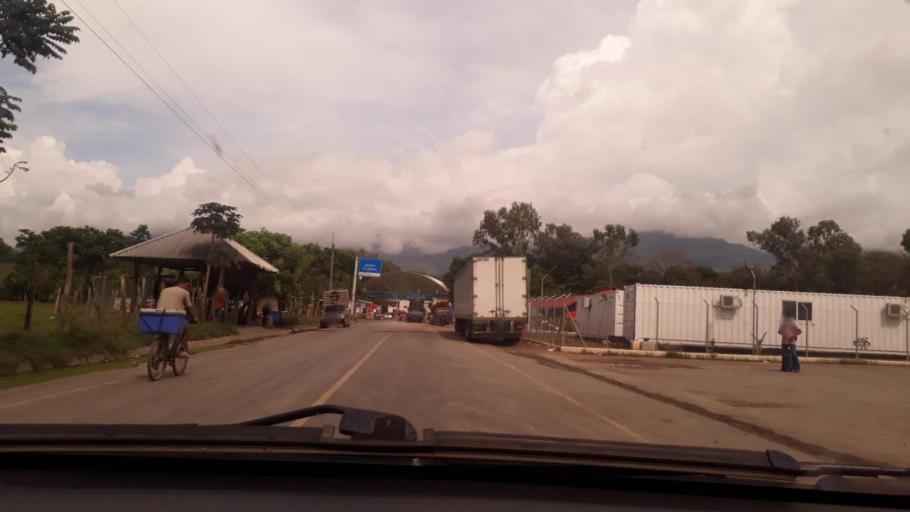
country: HN
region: Cortes
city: Potrerillos
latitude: 15.5968
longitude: -88.3735
